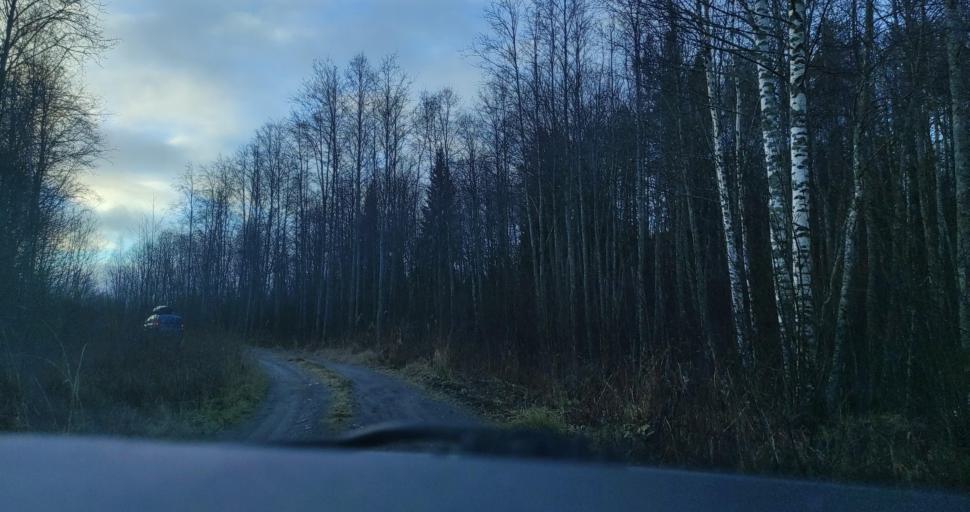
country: RU
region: Republic of Karelia
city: Pitkyaranta
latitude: 61.7305
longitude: 31.3799
